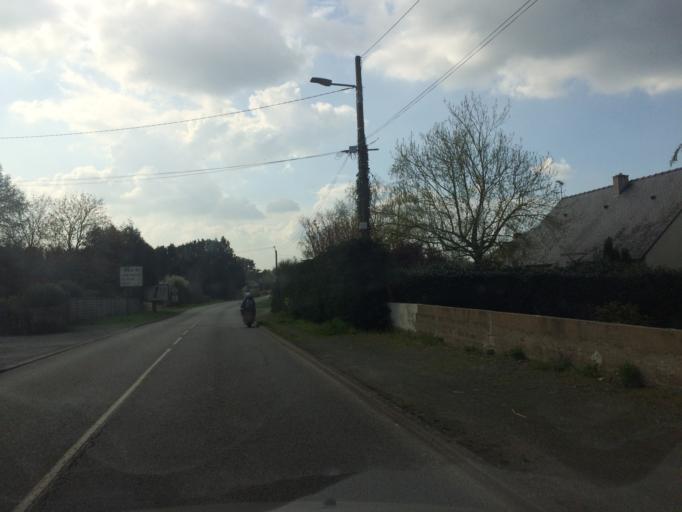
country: FR
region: Pays de la Loire
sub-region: Departement de la Loire-Atlantique
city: Blain
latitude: 47.4783
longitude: -1.7782
